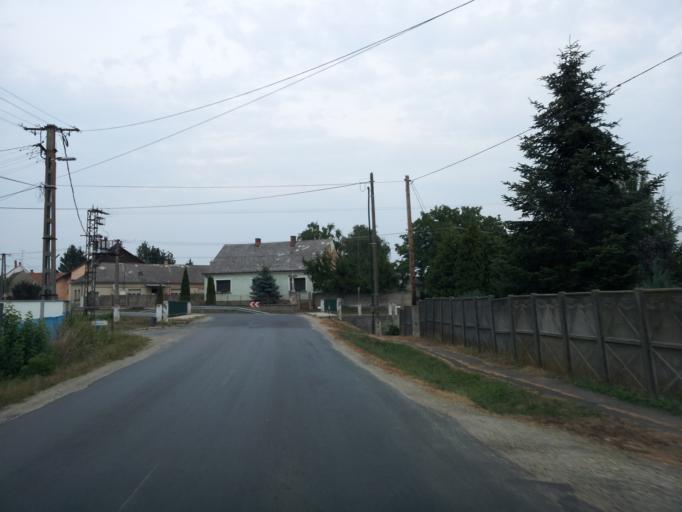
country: HU
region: Vas
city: Vep
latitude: 47.2048
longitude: 16.8187
